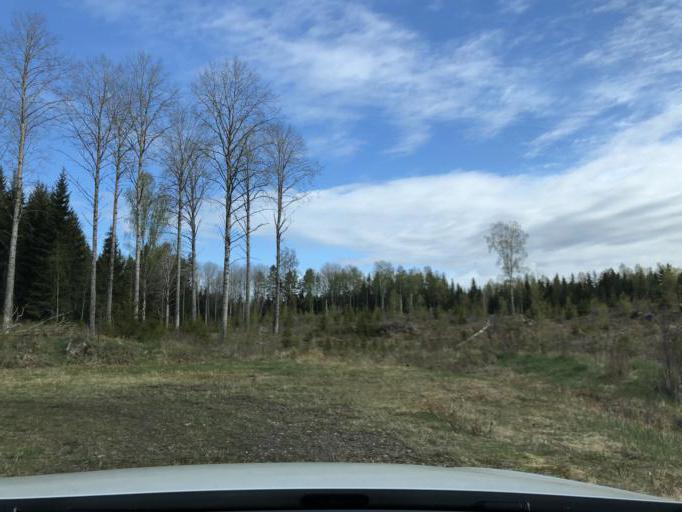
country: SE
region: Uppsala
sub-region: Heby Kommun
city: Tarnsjo
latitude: 60.2930
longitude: 16.8176
